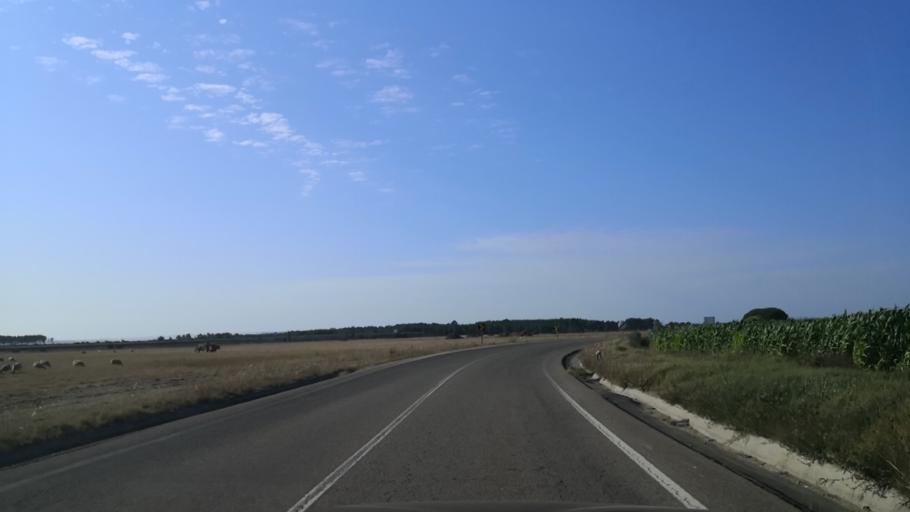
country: PT
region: Santarem
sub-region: Almeirim
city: Almeirim
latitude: 39.1547
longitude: -8.6200
